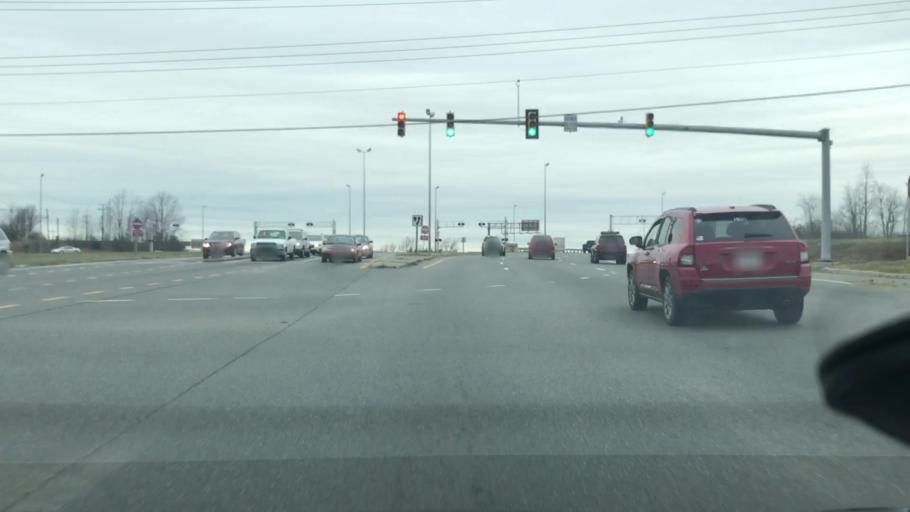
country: US
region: Virginia
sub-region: Montgomery County
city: Christiansburg
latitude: 37.1522
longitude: -80.4146
